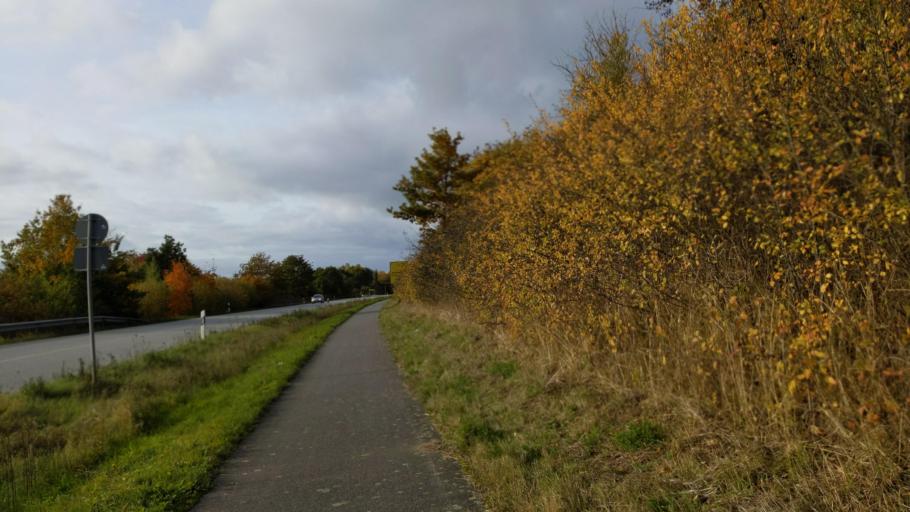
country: DE
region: Schleswig-Holstein
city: Eutin
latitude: 54.1161
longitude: 10.6188
